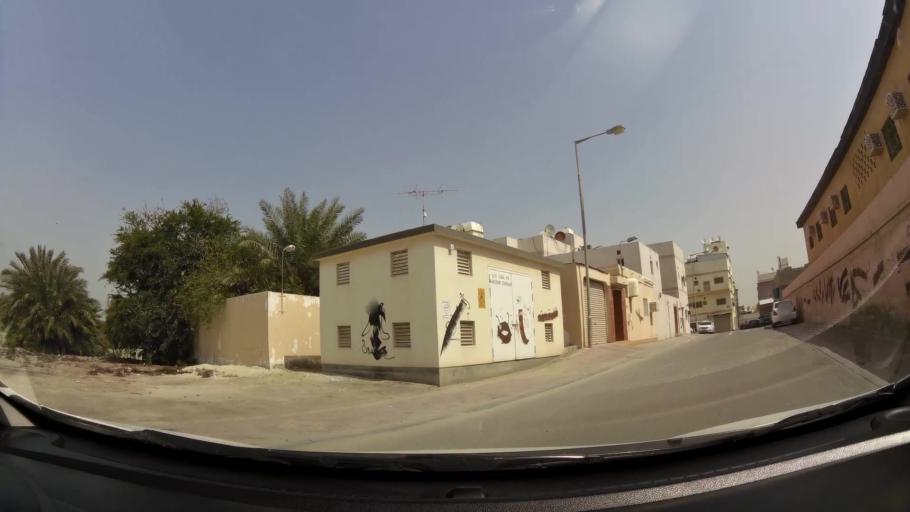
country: BH
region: Manama
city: Jidd Hafs
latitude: 26.2314
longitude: 50.4798
